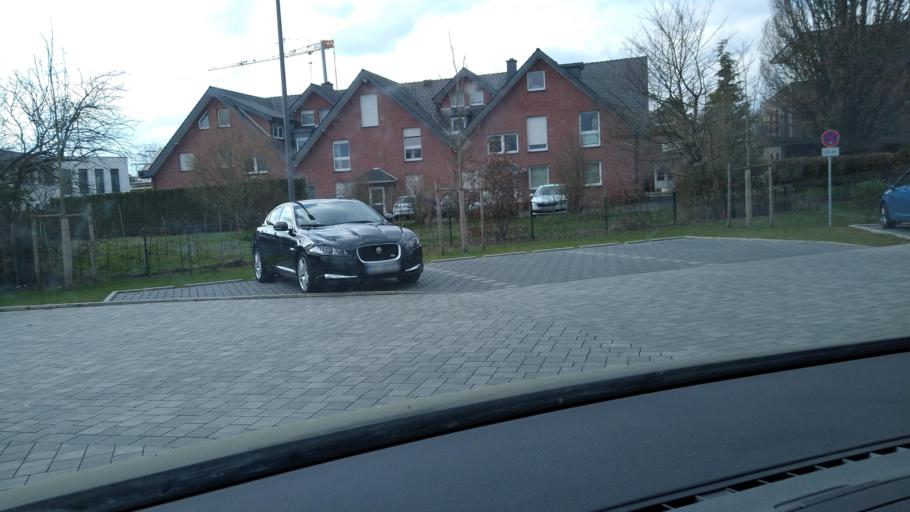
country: DE
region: North Rhine-Westphalia
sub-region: Regierungsbezirk Detmold
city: Verl
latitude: 51.8841
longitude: 8.5127
